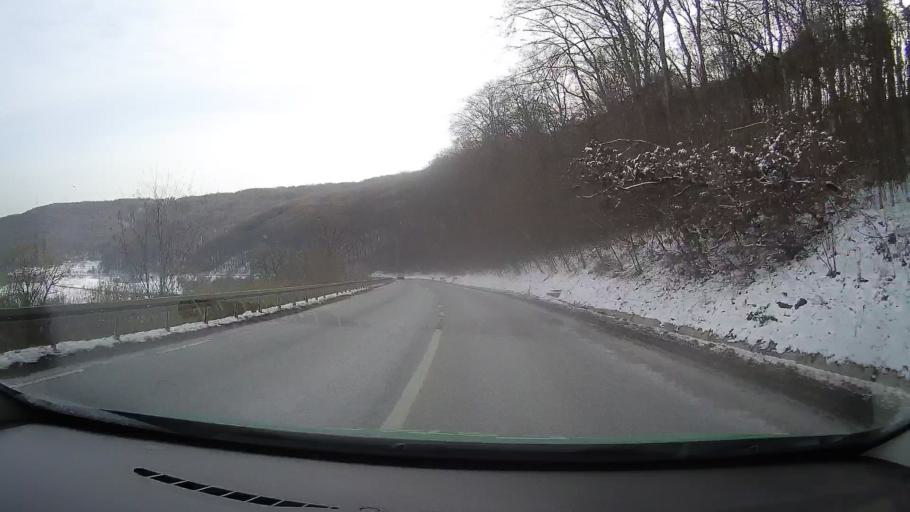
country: RO
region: Mures
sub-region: Municipiul Sighisoara
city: Sighisoara
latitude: 46.2220
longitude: 24.7558
